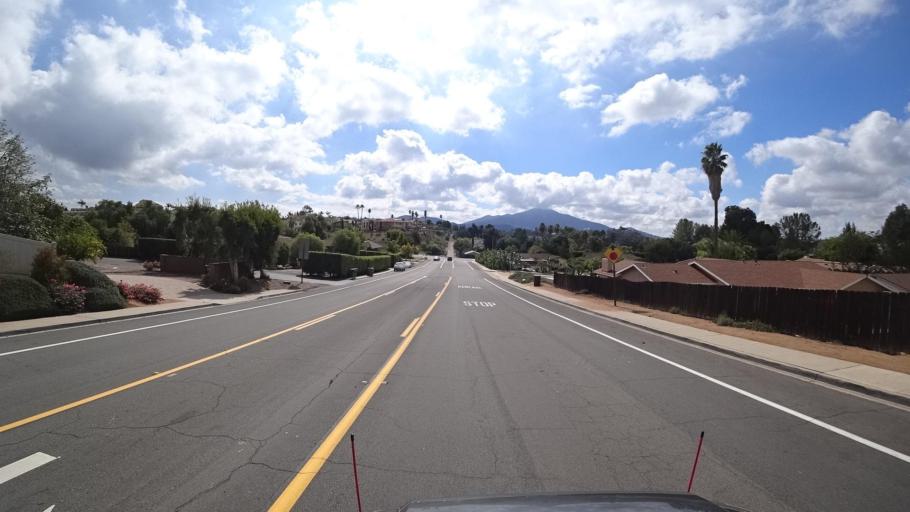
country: US
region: California
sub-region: San Diego County
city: Rancho San Diego
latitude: 32.7636
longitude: -116.9150
